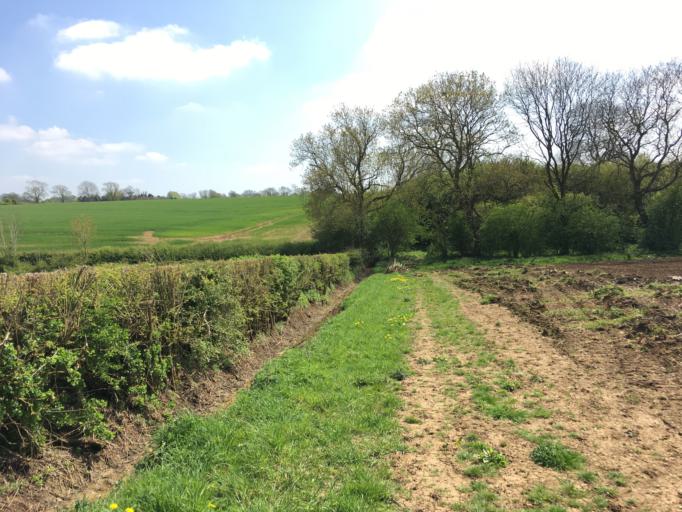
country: GB
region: England
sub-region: Leicestershire
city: Houghton on the Hill
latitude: 52.6086
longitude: -0.9850
